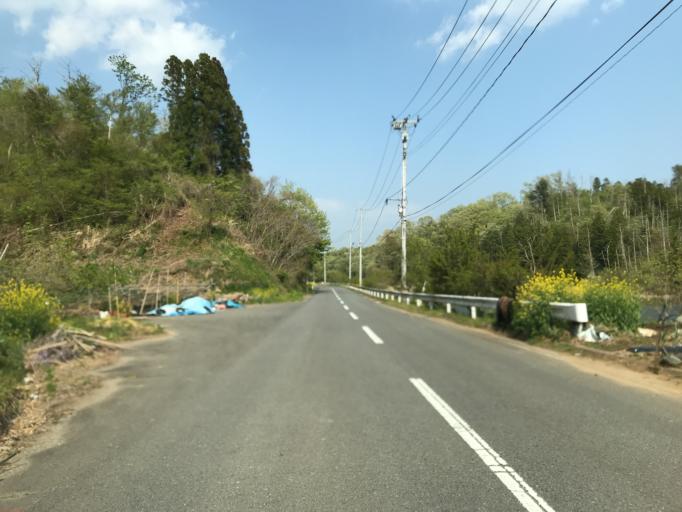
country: JP
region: Fukushima
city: Iwaki
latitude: 36.9943
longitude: 140.7672
